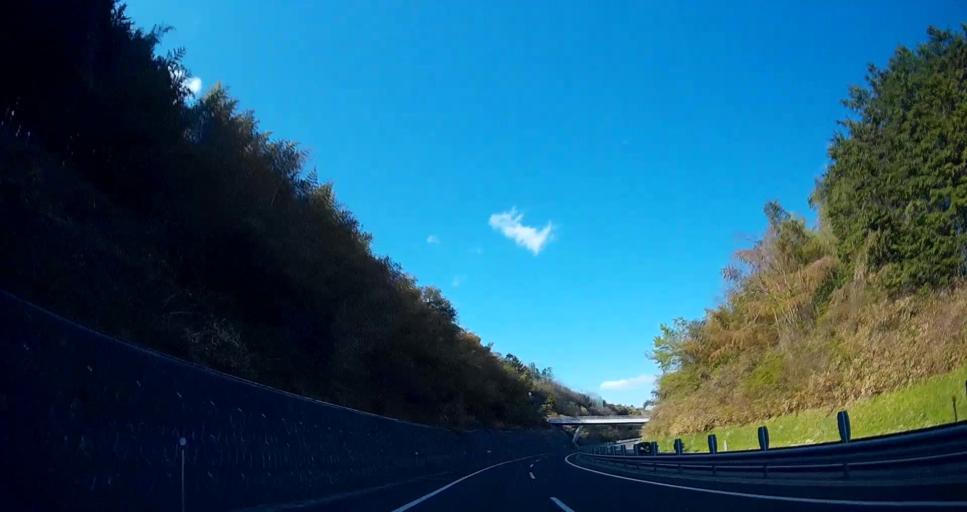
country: JP
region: Miyagi
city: Matsushima
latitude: 38.3859
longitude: 141.0339
